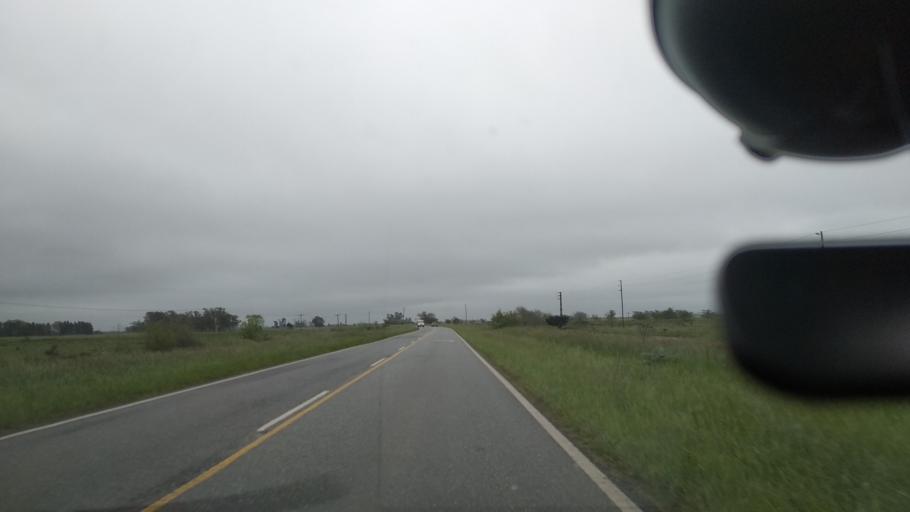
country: AR
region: Buenos Aires
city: Veronica
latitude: -35.3041
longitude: -57.4994
